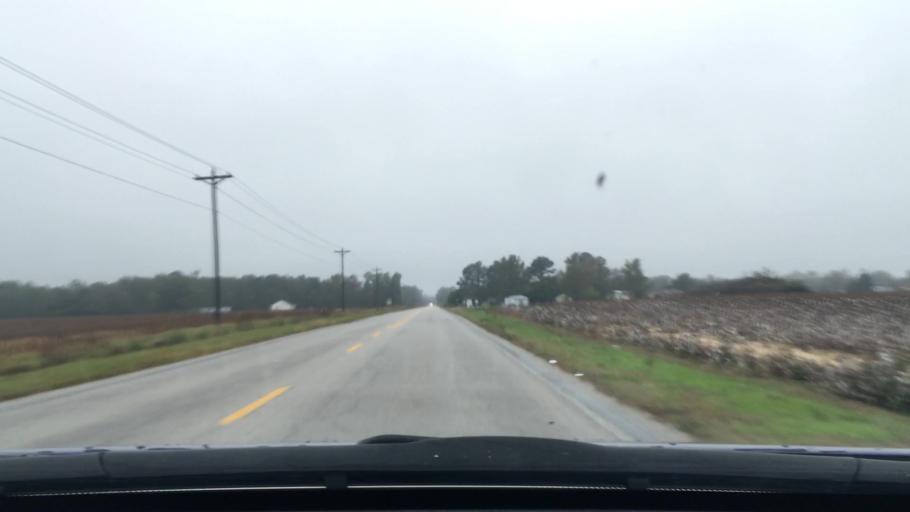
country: US
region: South Carolina
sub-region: Darlington County
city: Darlington
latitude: 34.2406
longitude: -79.9651
